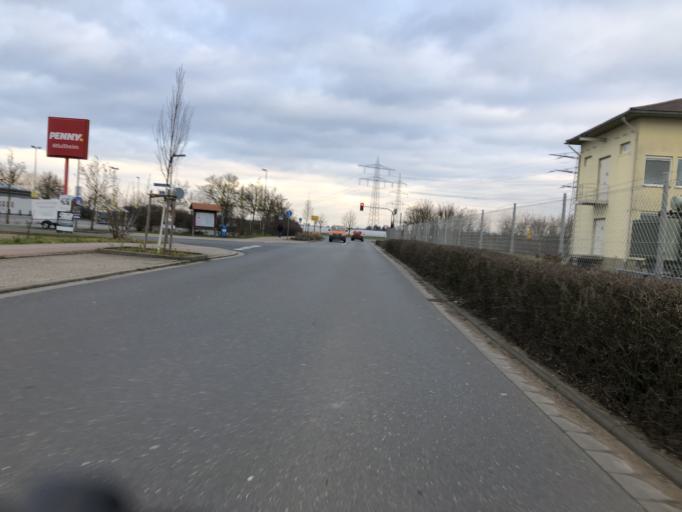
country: DE
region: Baden-Wuerttemberg
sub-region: Karlsruhe Region
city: Neulussheim
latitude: 49.2946
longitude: 8.5110
